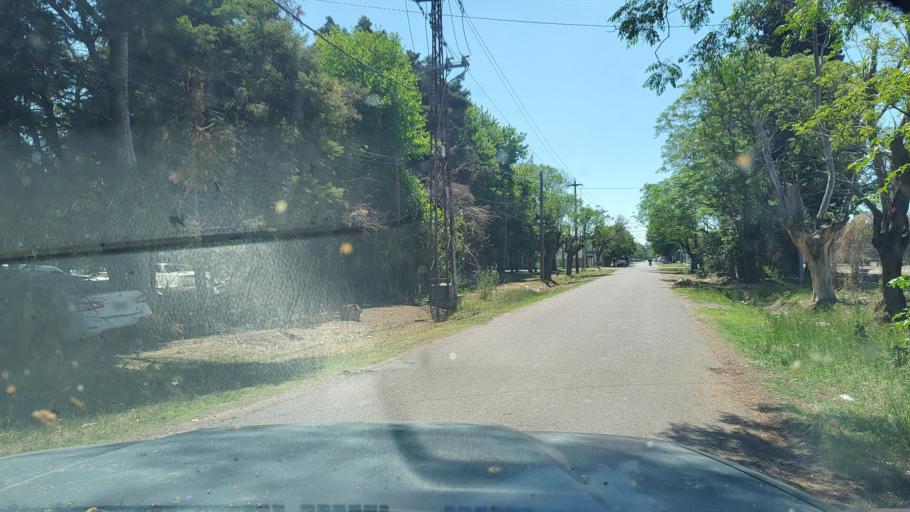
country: AR
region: Buenos Aires
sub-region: Partido de Lujan
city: Lujan
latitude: -34.6006
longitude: -59.1760
